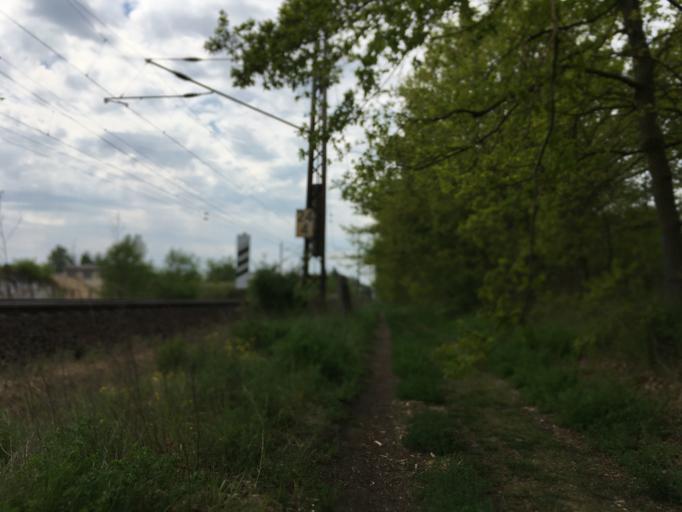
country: DE
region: Brandenburg
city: Bernau bei Berlin
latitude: 52.6892
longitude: 13.6073
